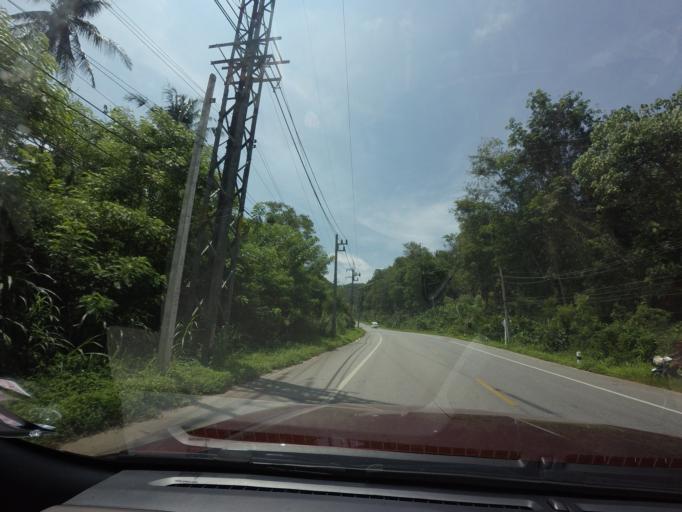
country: TH
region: Yala
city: Betong
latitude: 5.8186
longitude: 101.0985
